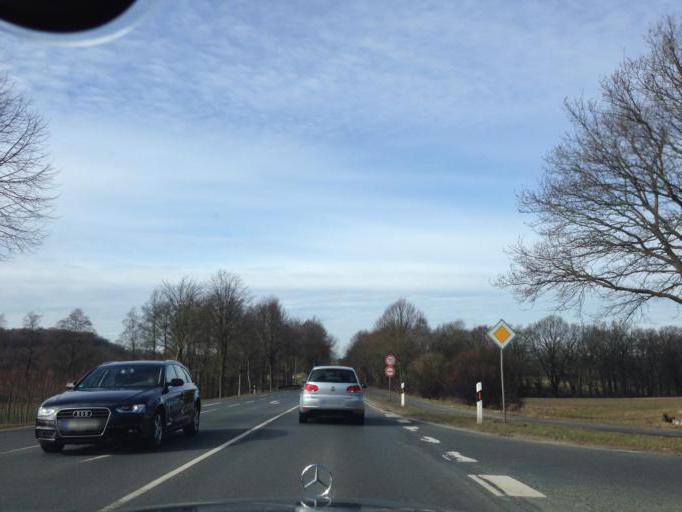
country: DE
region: Lower Saxony
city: Seevetal
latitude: 53.4373
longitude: 9.9148
